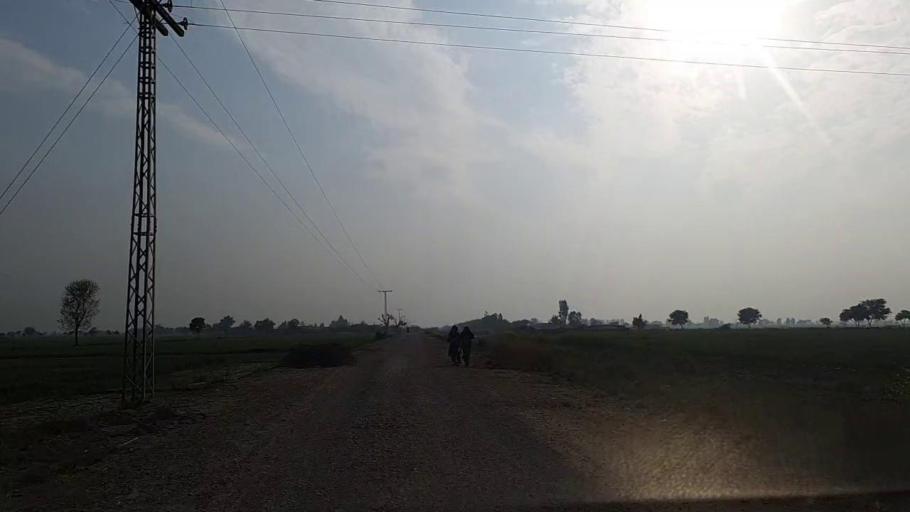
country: PK
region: Sindh
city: Jam Sahib
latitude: 26.3237
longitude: 68.5308
